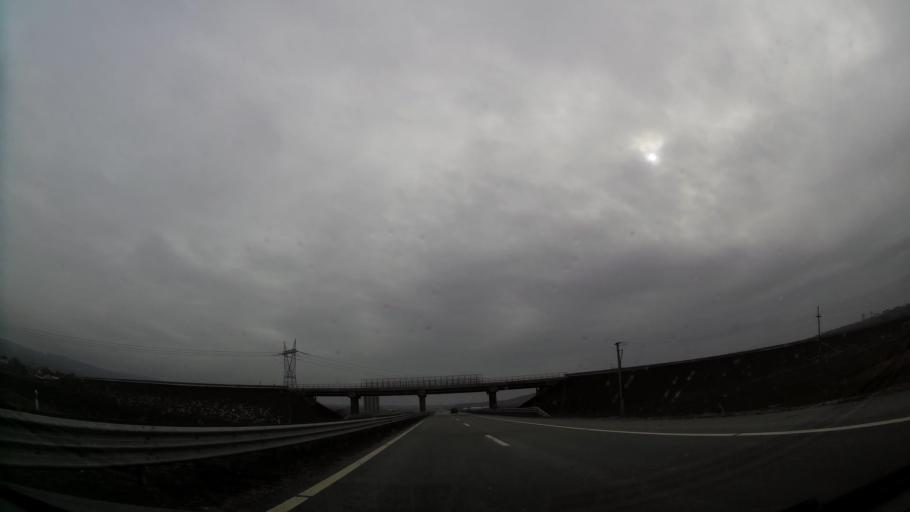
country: XK
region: Ferizaj
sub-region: Komuna e Ferizajt
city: Ferizaj
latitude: 42.4525
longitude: 21.1864
